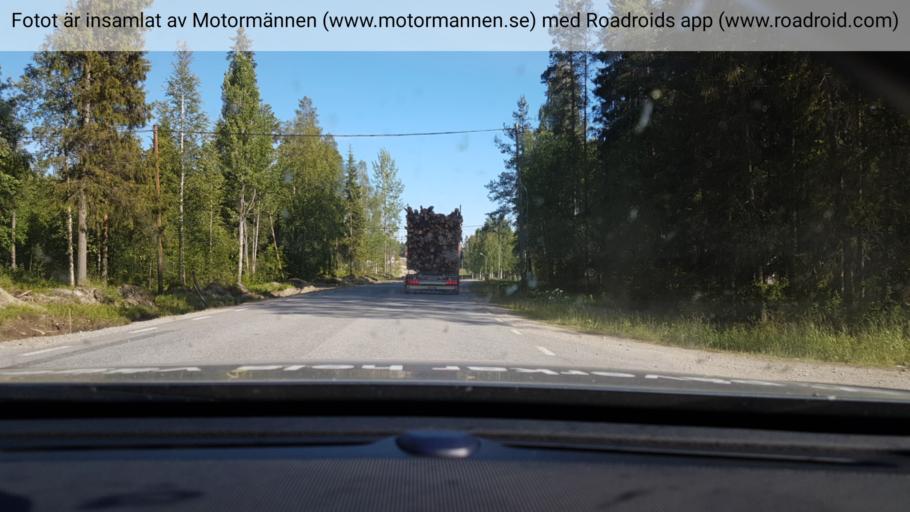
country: SE
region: Vaesterbotten
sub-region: Bjurholms Kommun
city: Bjurholm
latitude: 64.2320
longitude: 19.3513
